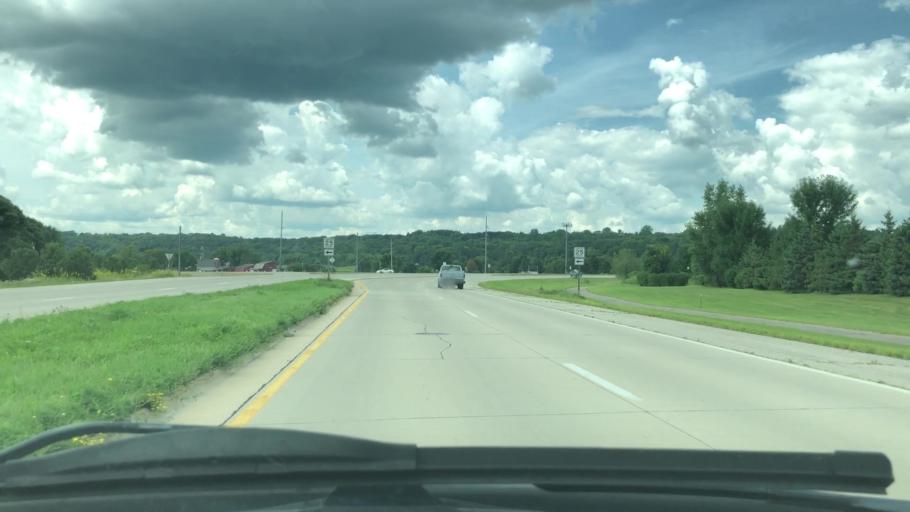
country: US
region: Minnesota
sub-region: Olmsted County
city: Rochester
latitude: 44.0032
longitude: -92.5055
